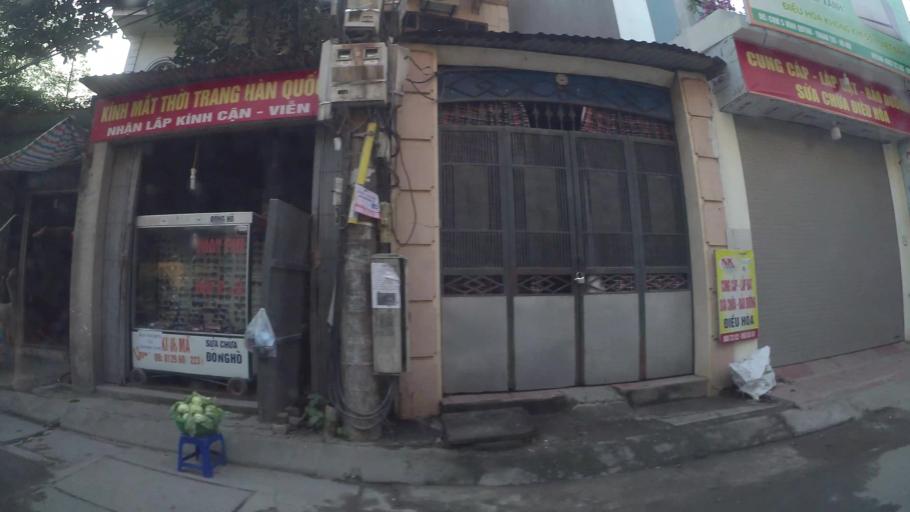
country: VN
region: Ha Noi
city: Van Dien
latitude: 20.9325
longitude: 105.8359
